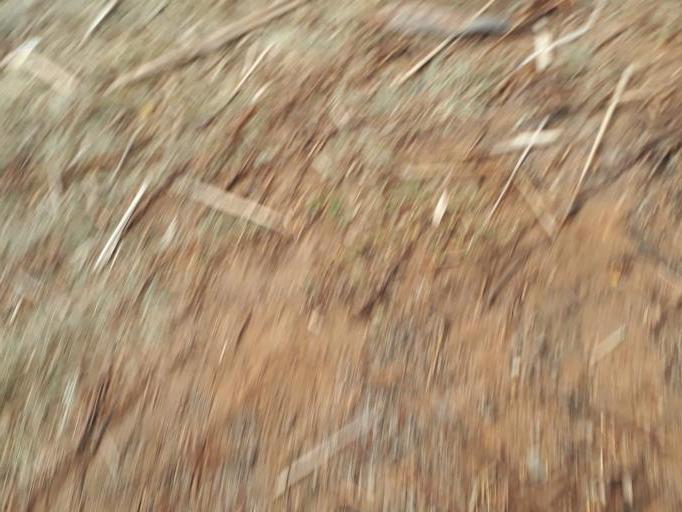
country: IN
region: Karnataka
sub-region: Mandya
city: Melukote
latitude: 12.6564
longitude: 76.6479
